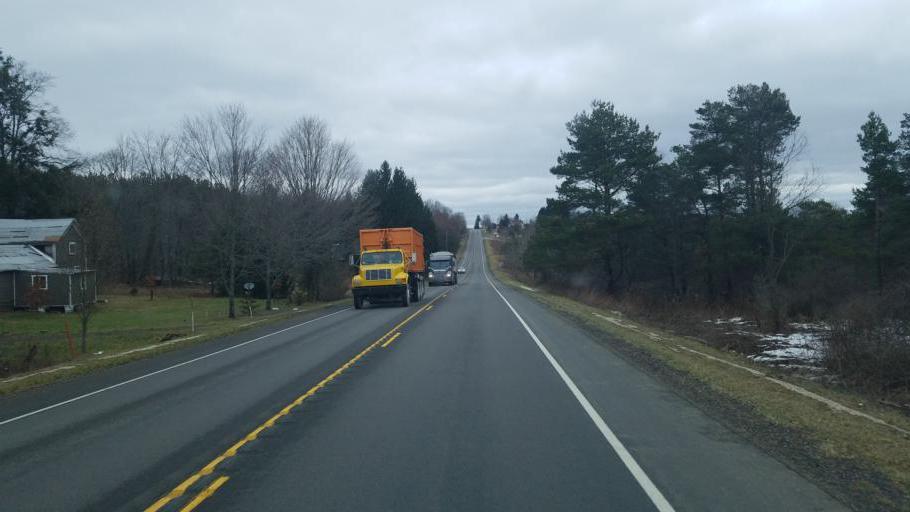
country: US
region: Pennsylvania
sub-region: Forest County
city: Marienville
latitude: 41.5311
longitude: -79.0495
